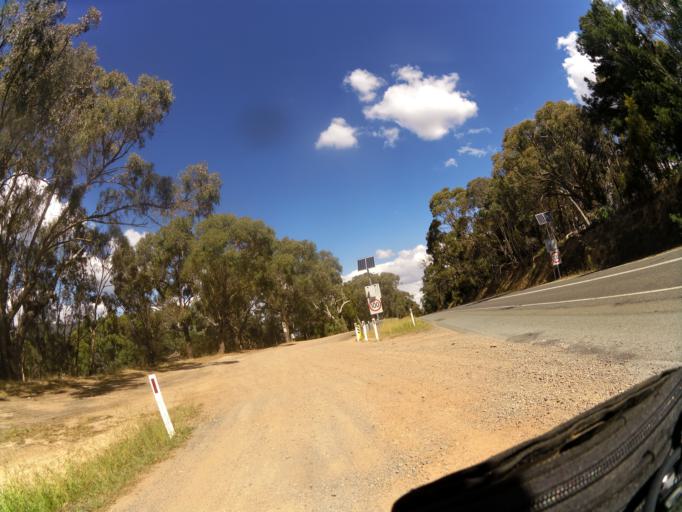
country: AU
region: Victoria
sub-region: Mansfield
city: Mansfield
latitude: -36.8398
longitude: 146.0073
